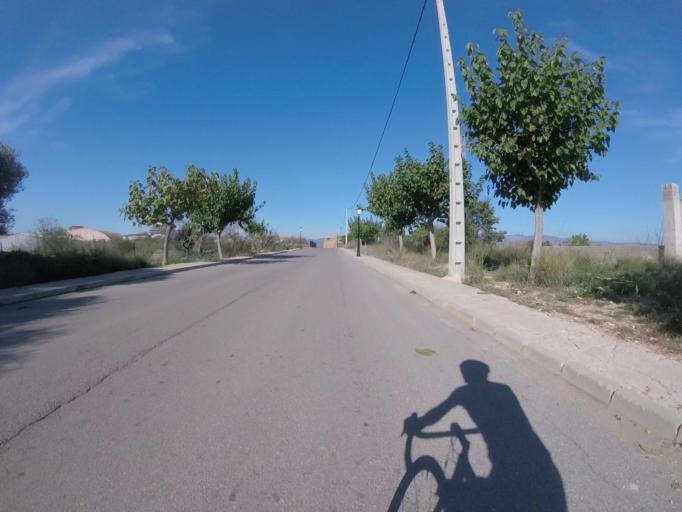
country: ES
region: Valencia
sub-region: Provincia de Castello
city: Benlloch
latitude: 40.2344
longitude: 0.0757
